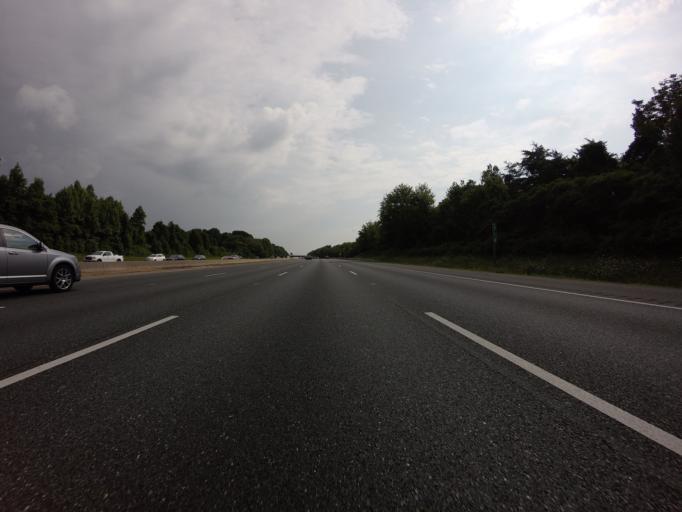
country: US
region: Maryland
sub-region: Baltimore County
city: Kingsville
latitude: 39.4252
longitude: -76.3927
